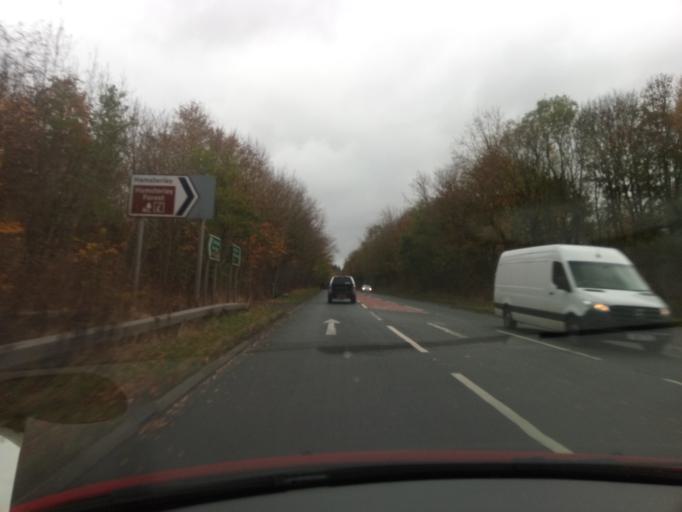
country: GB
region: England
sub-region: County Durham
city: High Etherley
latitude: 54.6706
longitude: -1.7758
